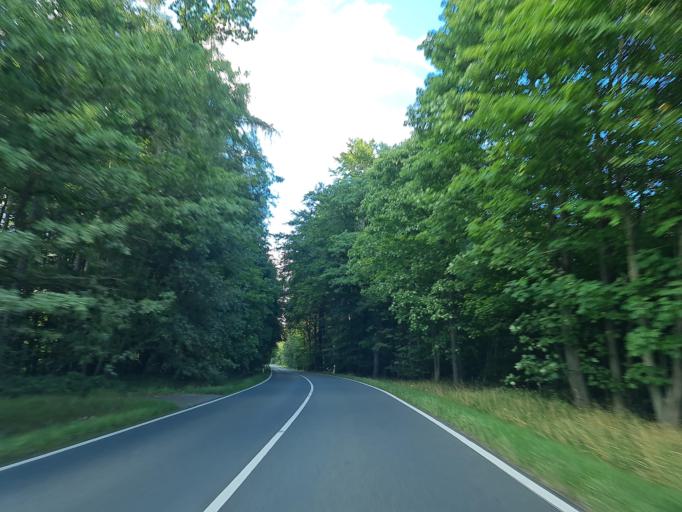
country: DE
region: Saxony
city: Pausa
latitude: 50.6027
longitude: 11.9974
